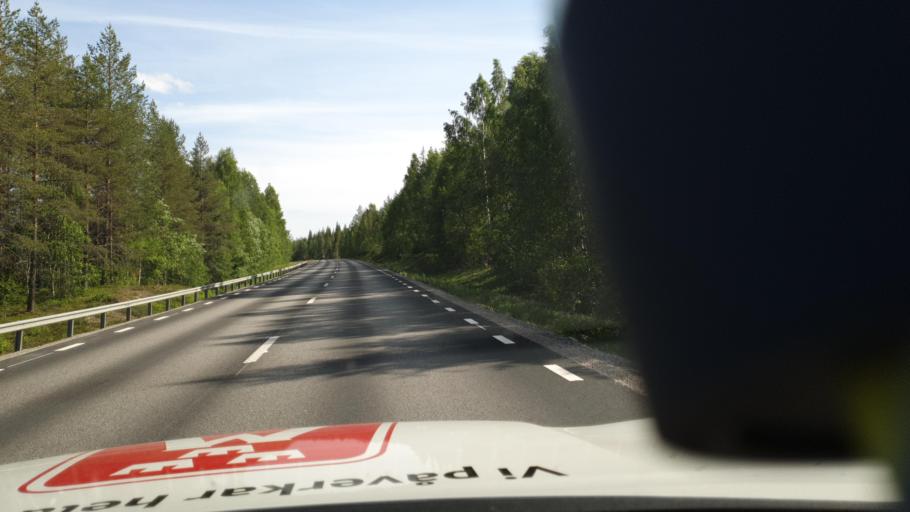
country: SE
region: Vaesterbotten
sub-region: Skelleftea Kommun
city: Boliden
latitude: 64.8936
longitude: 20.3749
